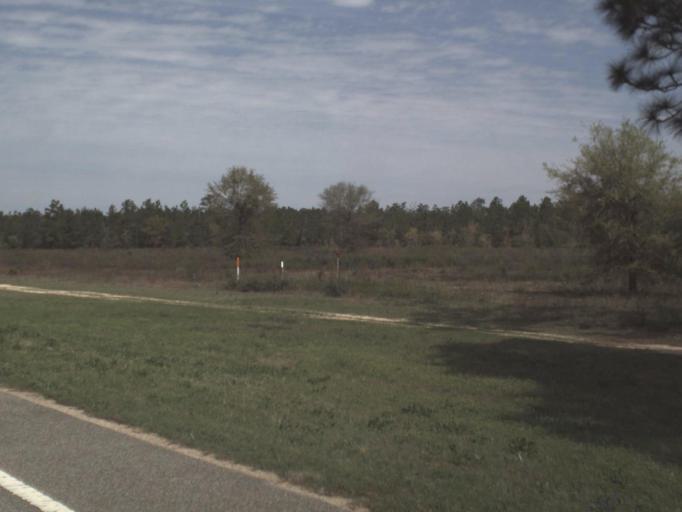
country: US
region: Florida
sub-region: Okaloosa County
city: Crestview
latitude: 30.7480
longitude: -86.4219
